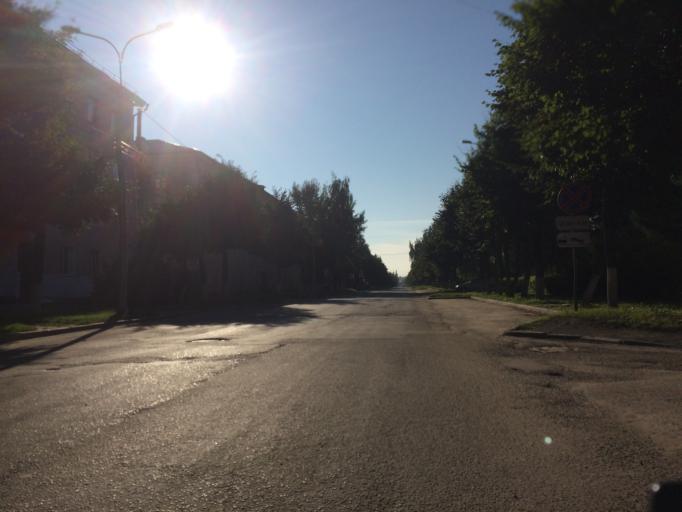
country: RU
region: Mariy-El
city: Yoshkar-Ola
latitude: 56.6411
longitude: 47.8819
